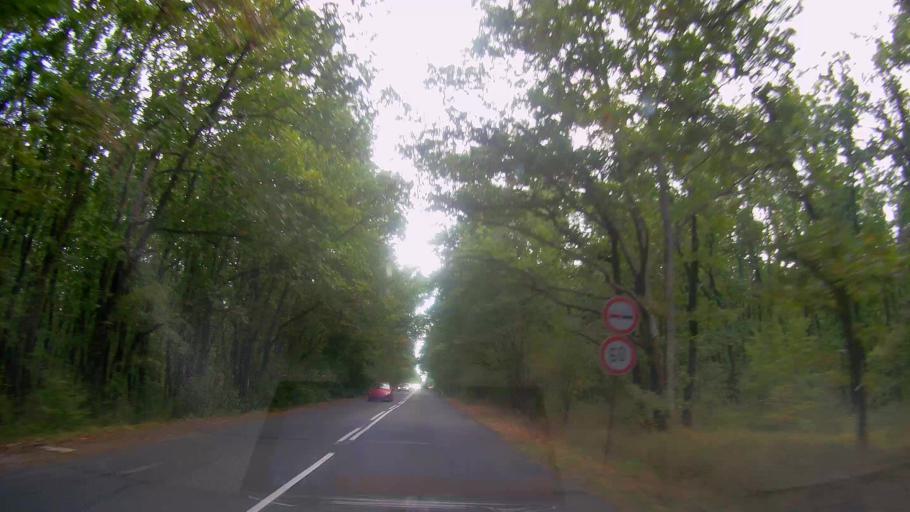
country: BG
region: Burgas
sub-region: Obshtina Primorsko
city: Primorsko
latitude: 42.2791
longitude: 27.7390
